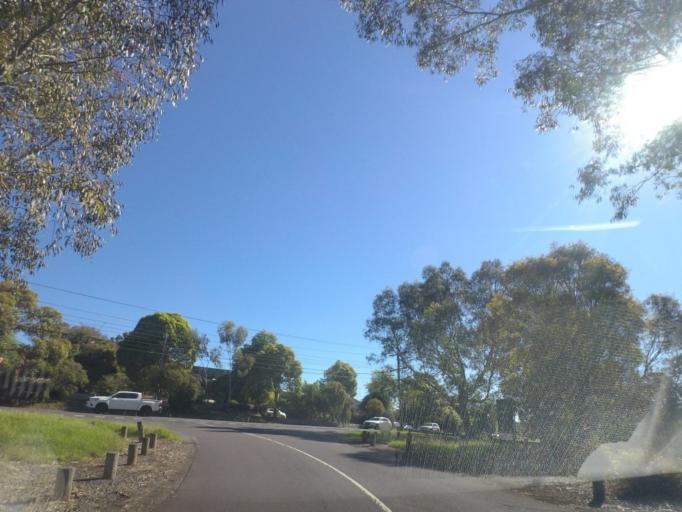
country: AU
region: Victoria
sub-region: Banyule
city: Viewbank
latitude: -37.7551
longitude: 145.0953
